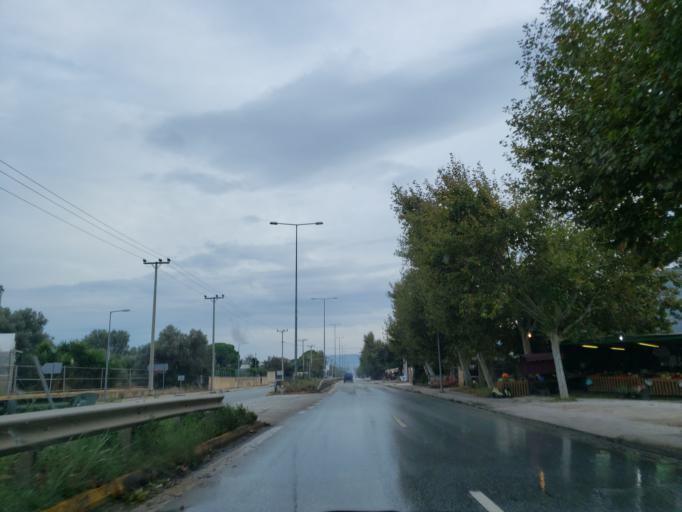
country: GR
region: Attica
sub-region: Nomarchia Anatolikis Attikis
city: Aghios Panteleimon
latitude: 38.1160
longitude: 23.9698
